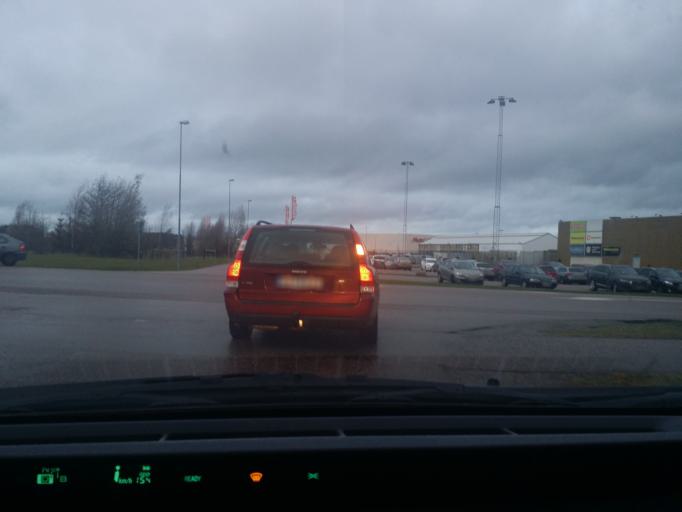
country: SE
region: Soedermanland
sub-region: Eskilstuna Kommun
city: Eskilstuna
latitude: 59.3716
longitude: 16.4673
